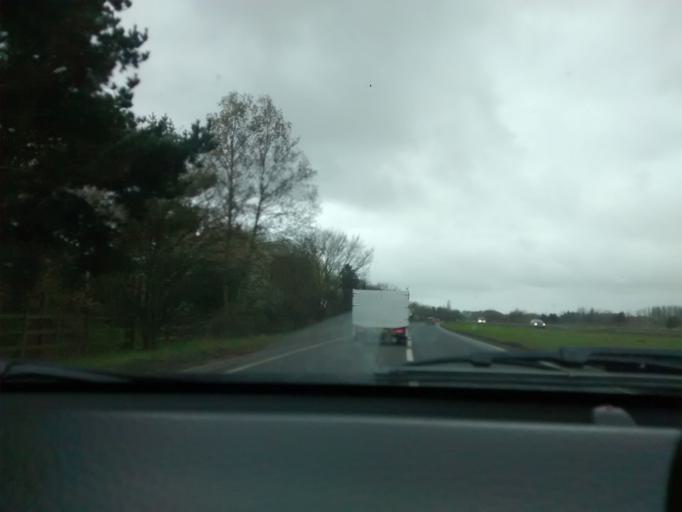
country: GB
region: England
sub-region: Suffolk
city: Felixstowe
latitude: 51.9806
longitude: 1.3276
